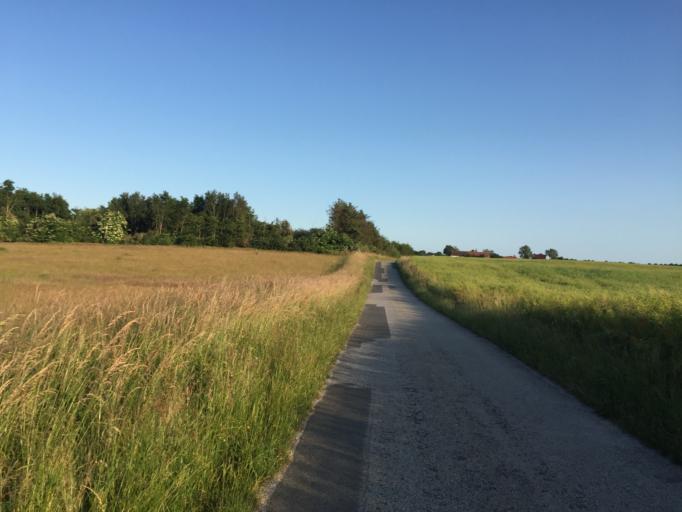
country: DK
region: Zealand
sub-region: Slagelse Kommune
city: Skaelskor
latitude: 55.2231
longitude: 11.1843
